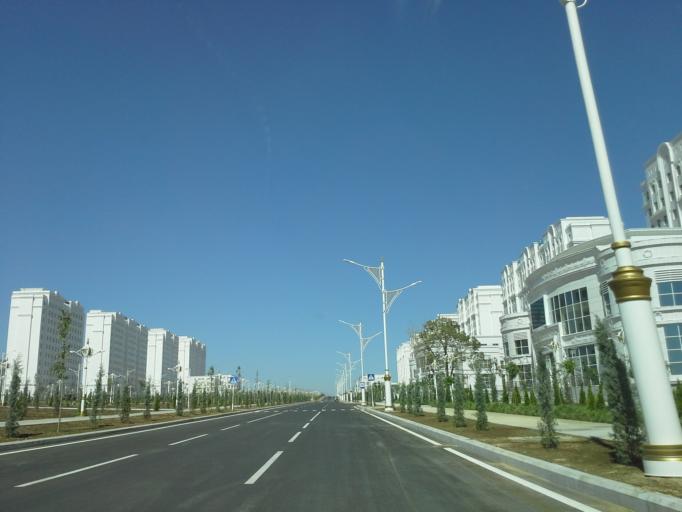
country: TM
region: Ahal
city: Ashgabat
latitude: 37.9410
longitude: 58.3547
